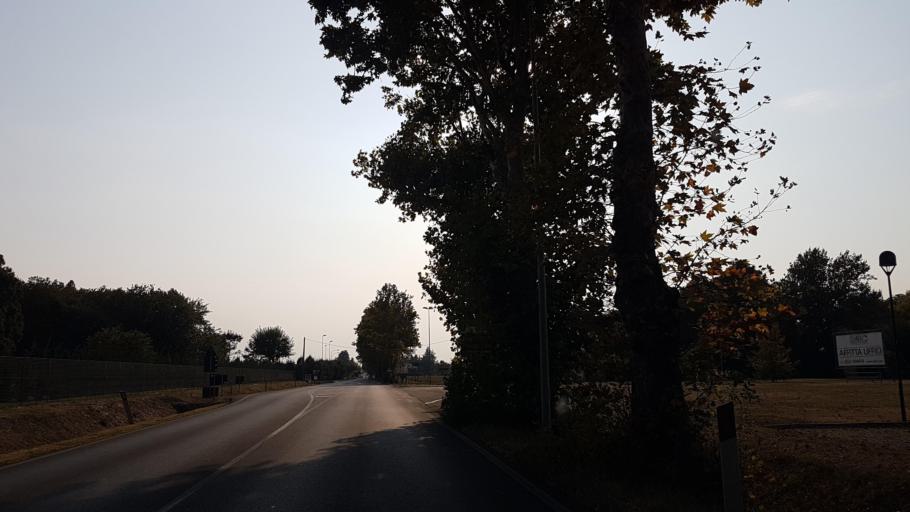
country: IT
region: Emilia-Romagna
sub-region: Provincia di Parma
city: Vicofertile
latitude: 44.7668
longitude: 10.2552
